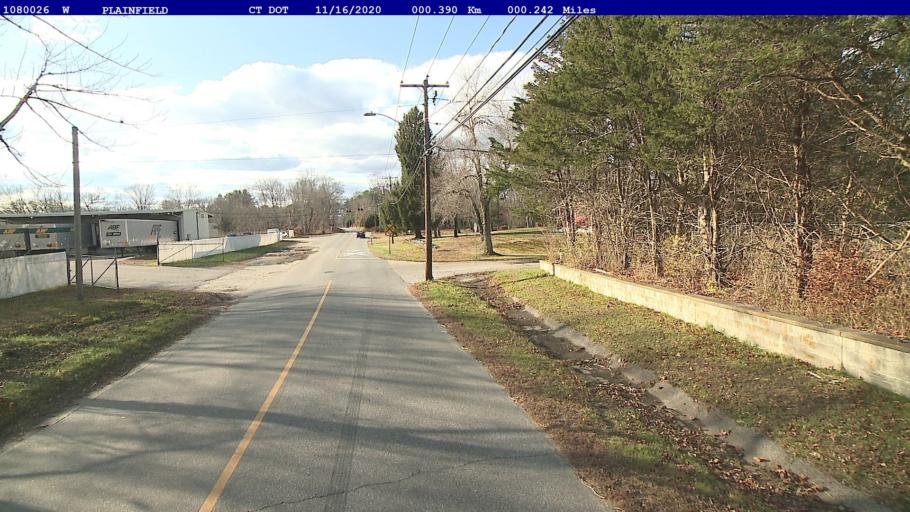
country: US
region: Connecticut
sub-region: Windham County
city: Plainfield
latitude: 41.6871
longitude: -71.9187
